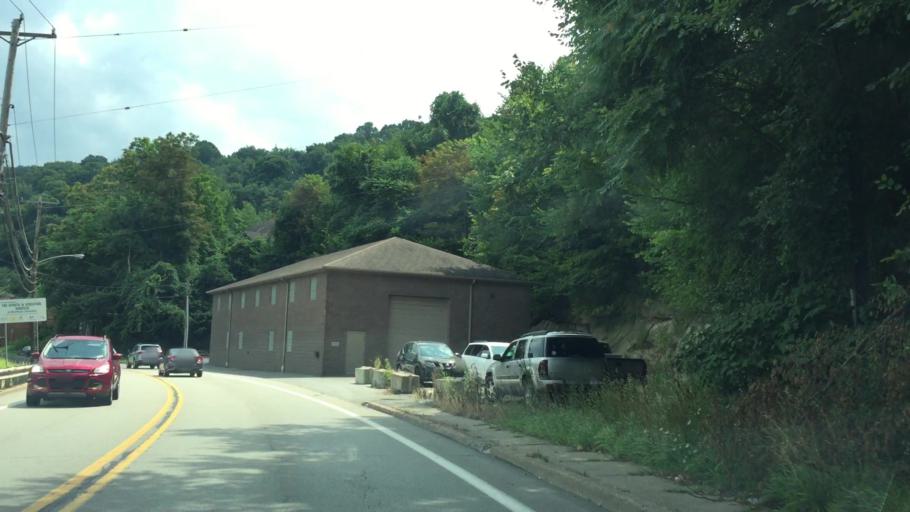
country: US
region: Pennsylvania
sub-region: Allegheny County
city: Coraopolis
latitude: 40.5081
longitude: -80.1506
